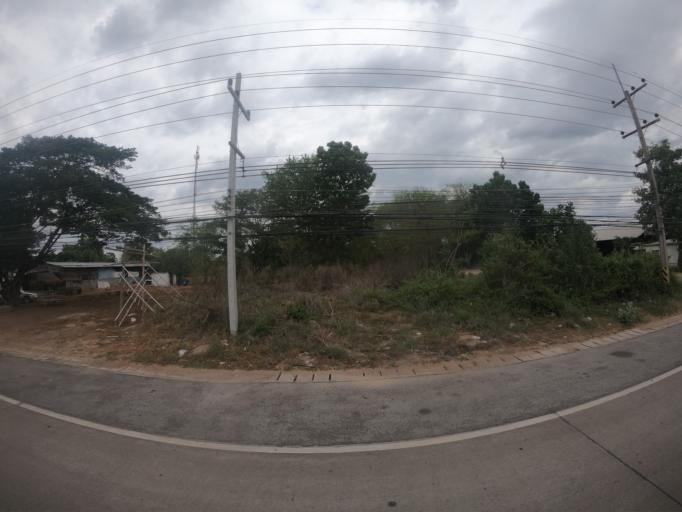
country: TH
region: Nakhon Ratchasima
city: Chok Chai
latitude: 14.7488
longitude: 102.1644
